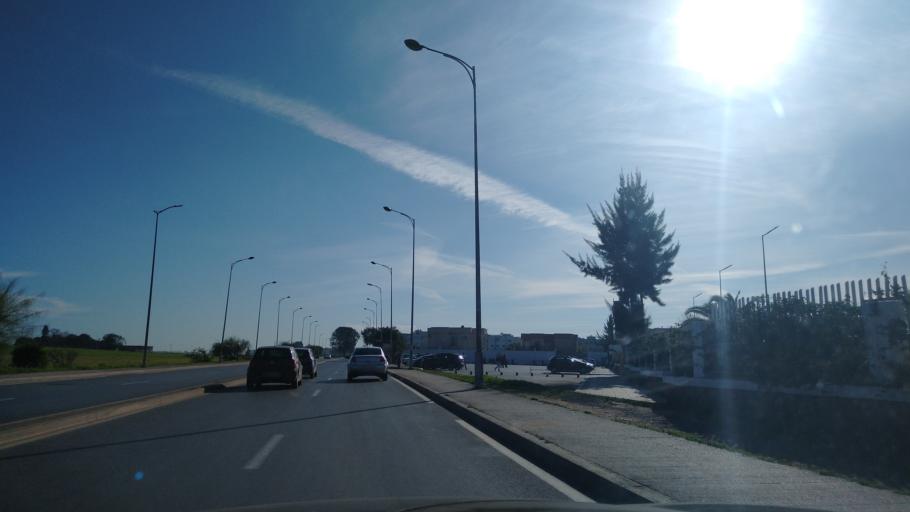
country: MA
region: Rabat-Sale-Zemmour-Zaer
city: Sale
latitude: 34.0203
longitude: -6.7348
